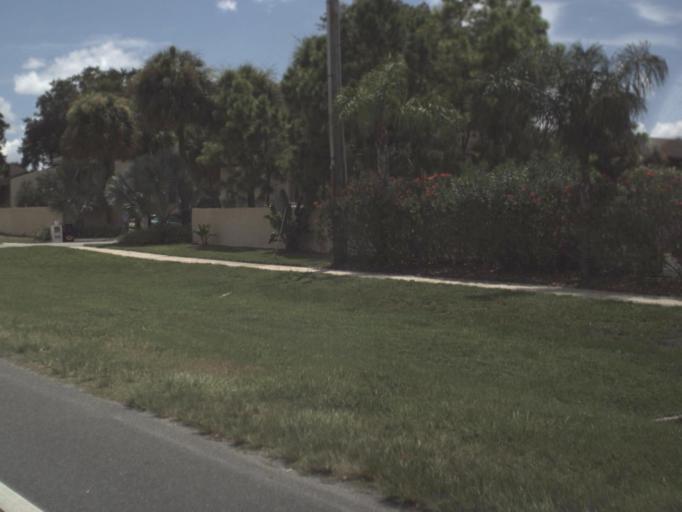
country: US
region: Florida
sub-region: Hillsborough County
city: Egypt Lake-Leto
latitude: 28.0312
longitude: -82.5051
